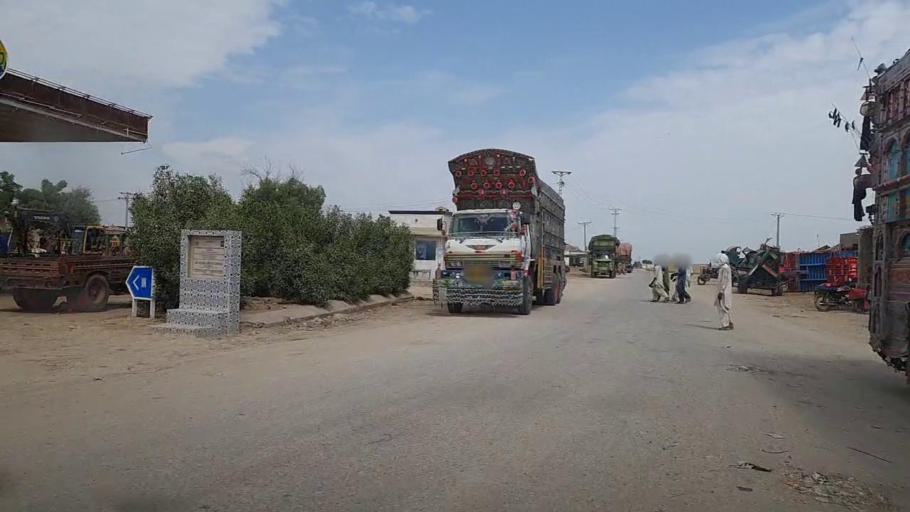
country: PK
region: Sindh
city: Thul
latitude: 28.2561
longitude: 68.7699
